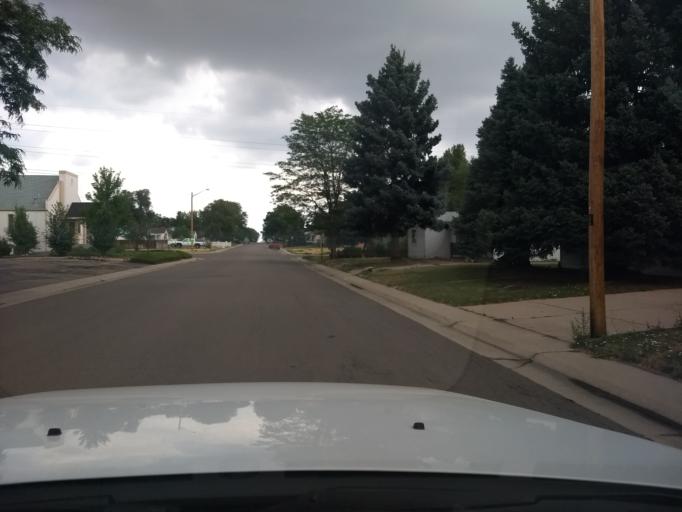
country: US
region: Colorado
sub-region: Arapahoe County
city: Sheridan
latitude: 39.6979
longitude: -105.0204
